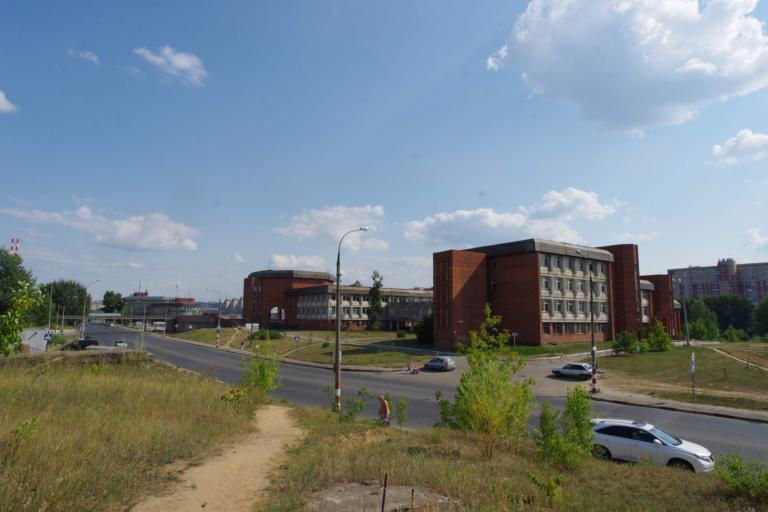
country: RU
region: Nizjnij Novgorod
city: Nizhniy Novgorod
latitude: 56.3423
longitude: 43.9385
